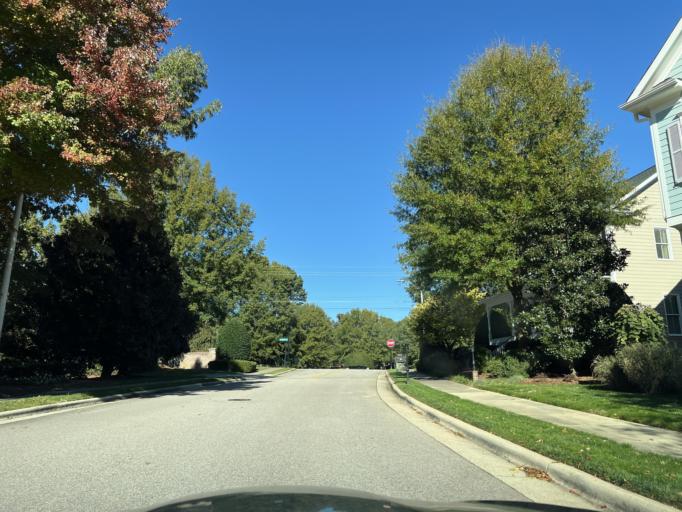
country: US
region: North Carolina
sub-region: Wake County
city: West Raleigh
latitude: 35.8964
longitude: -78.6454
